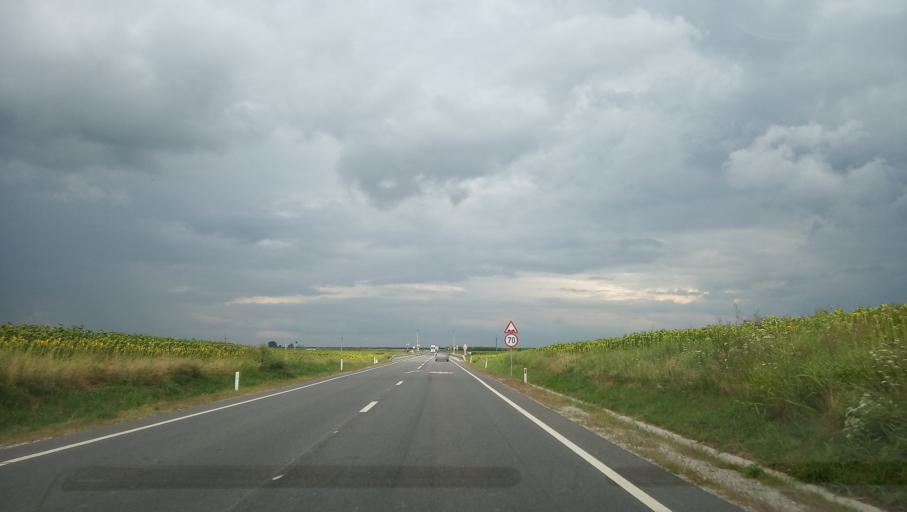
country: RO
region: Olt
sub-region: Comuna Deveselu
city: Comanca
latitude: 44.0931
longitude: 24.3738
